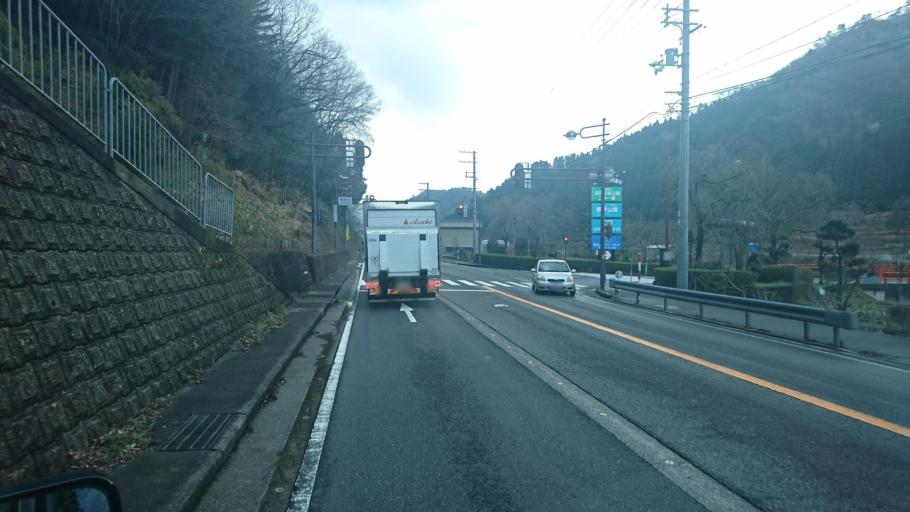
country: JP
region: Tottori
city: Tottori
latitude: 35.5507
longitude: 134.4947
